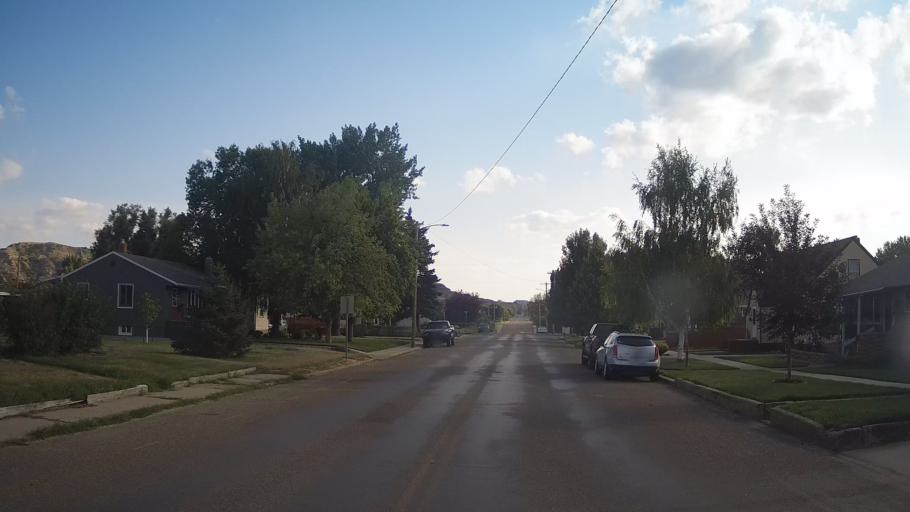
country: US
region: Montana
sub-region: Dawson County
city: Glendive
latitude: 47.0960
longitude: -104.7119
